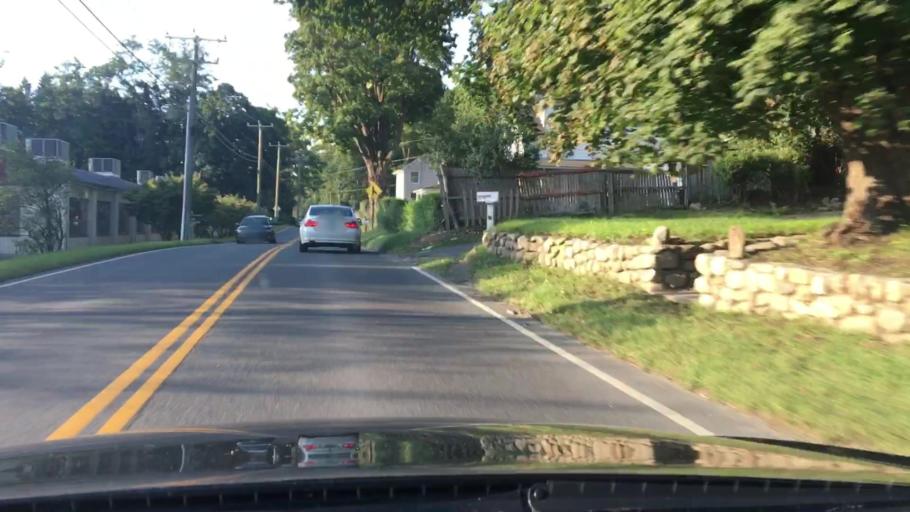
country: US
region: Connecticut
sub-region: Litchfield County
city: New Milford
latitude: 41.5669
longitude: -73.4054
